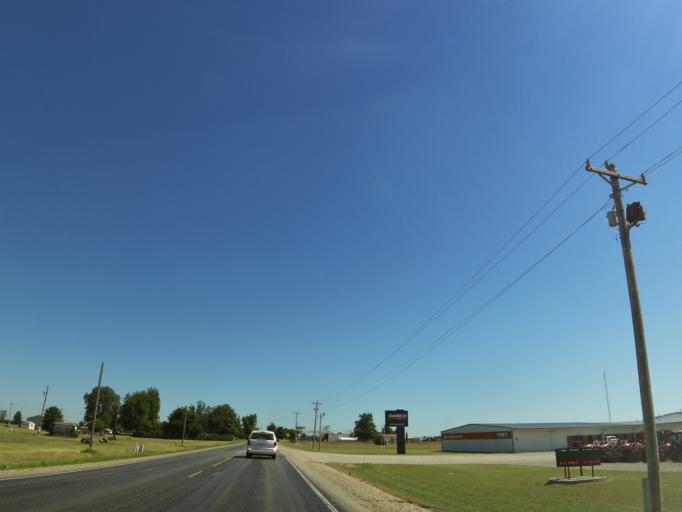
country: US
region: Missouri
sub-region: Dunklin County
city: Malden
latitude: 36.5245
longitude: -89.9709
